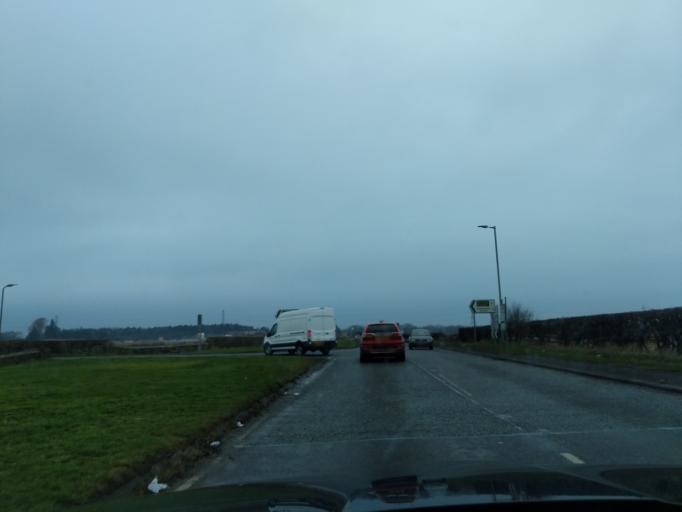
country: GB
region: England
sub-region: Northumberland
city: Stannington
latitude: 55.1304
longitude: -1.6449
